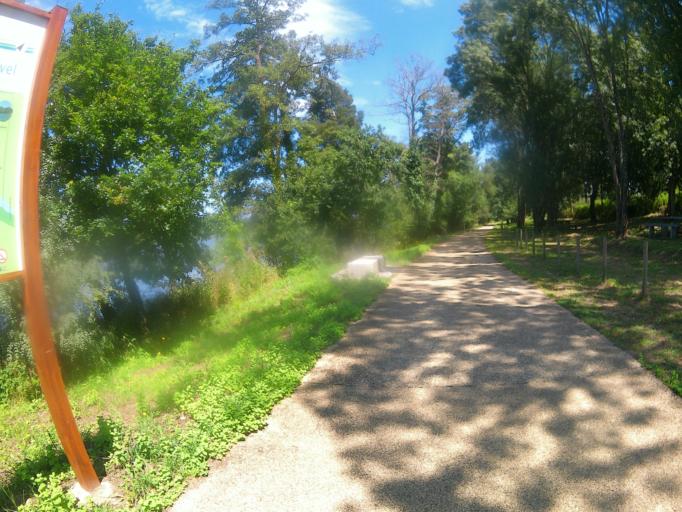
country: ES
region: Galicia
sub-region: Provincia de Pontevedra
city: Tomino
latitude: 41.9687
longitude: -8.7348
